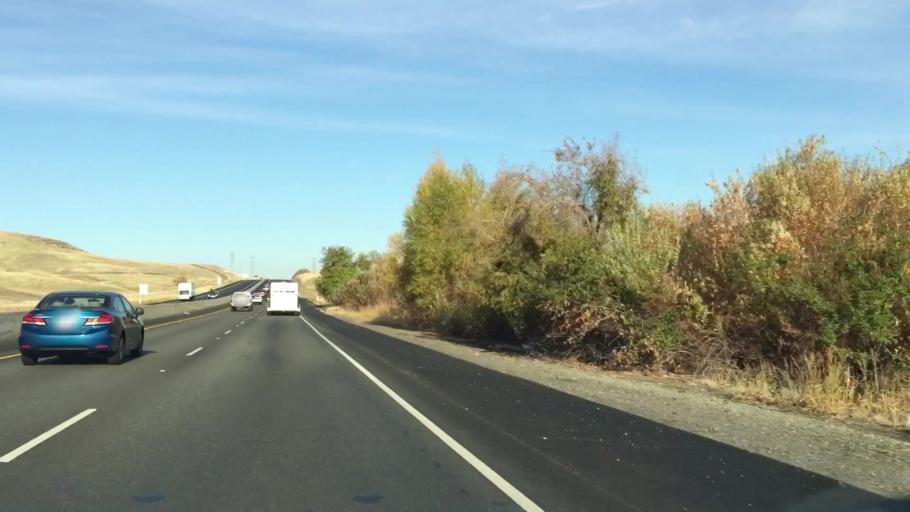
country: US
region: California
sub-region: Butte County
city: Thermalito
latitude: 39.5384
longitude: -121.5856
